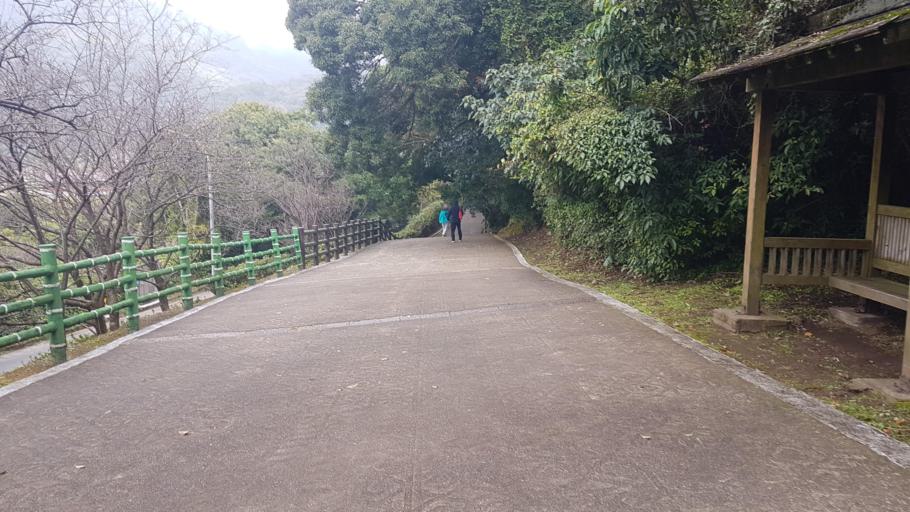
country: TW
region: Taipei
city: Taipei
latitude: 25.1533
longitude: 121.5393
